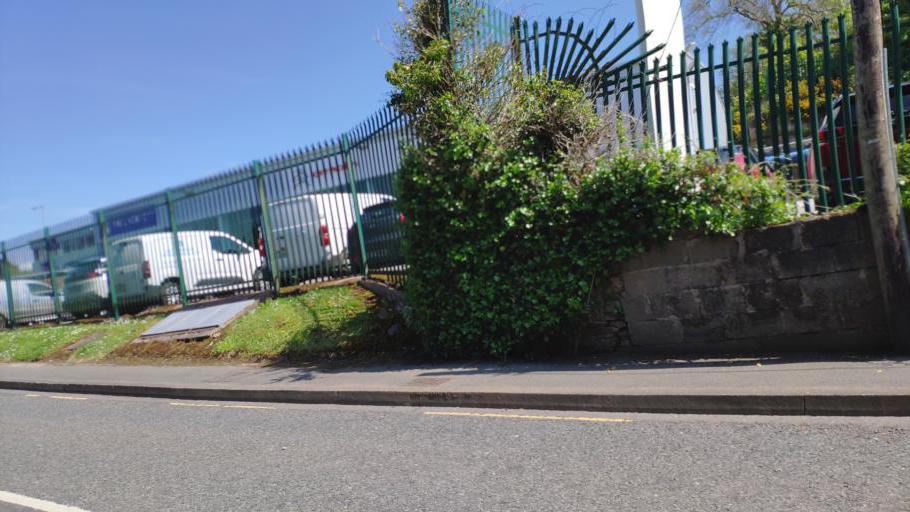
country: IE
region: Munster
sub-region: County Cork
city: Cork
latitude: 51.9271
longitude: -8.4899
